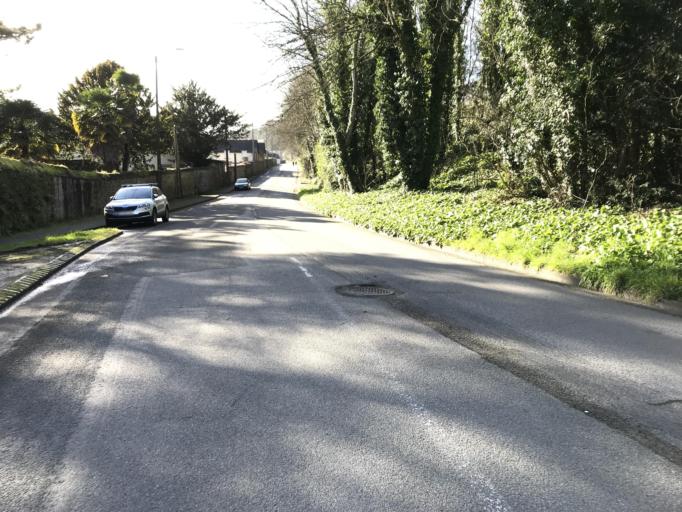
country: FR
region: Brittany
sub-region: Departement du Finistere
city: Brest
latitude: 48.3933
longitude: -4.4424
